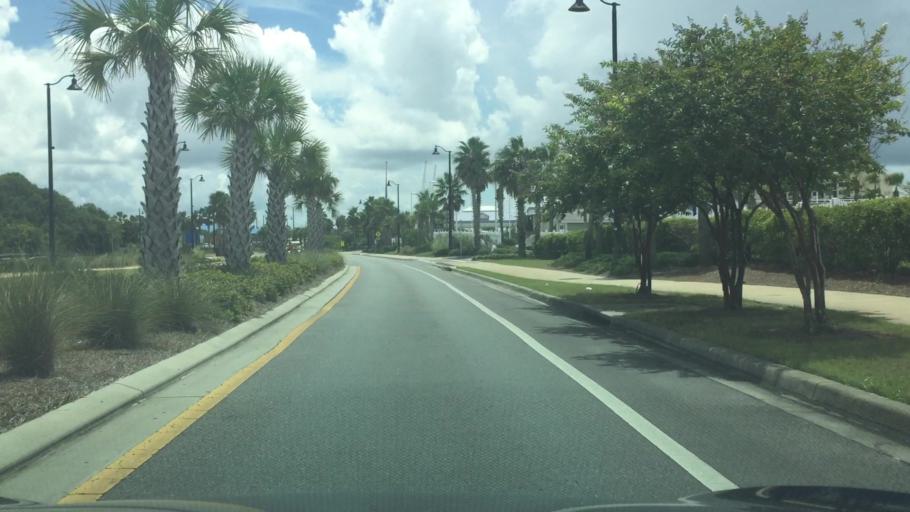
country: US
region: Florida
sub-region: Bay County
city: Panama City Beach
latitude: 30.1725
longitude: -85.7981
